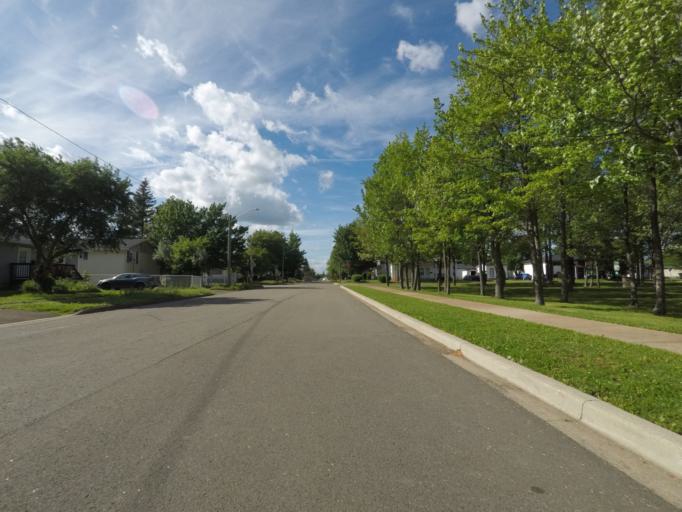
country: CA
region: New Brunswick
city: Moncton
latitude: 46.1000
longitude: -64.8252
